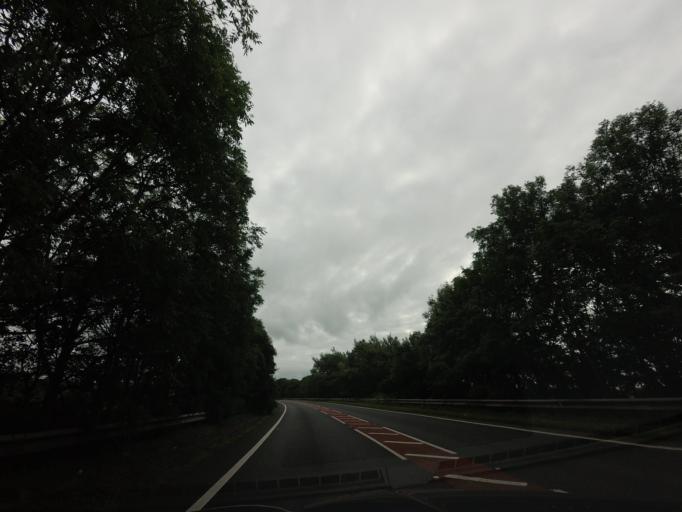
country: GB
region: Scotland
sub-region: Dumfries and Galloway
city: Gretna
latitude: 54.9924
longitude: -3.1133
